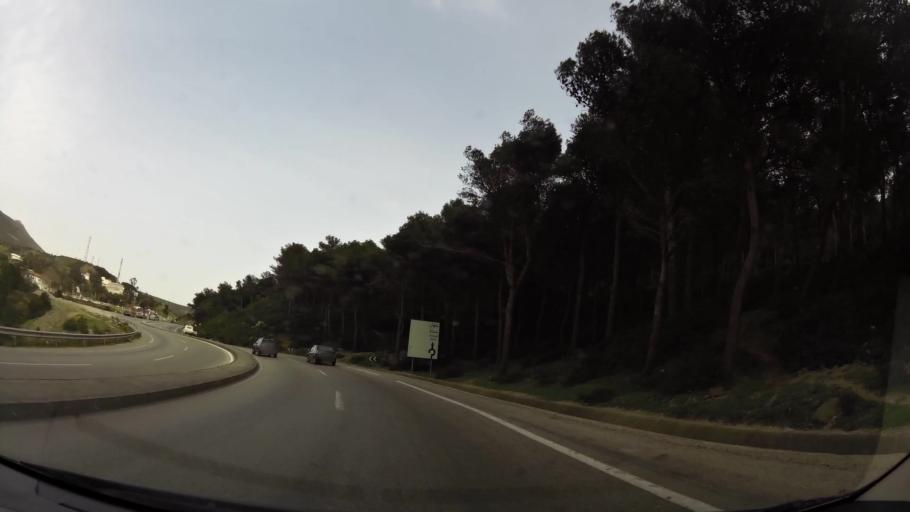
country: MA
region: Tanger-Tetouan
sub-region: Tetouan
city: Saddina
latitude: 35.5603
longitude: -5.5780
